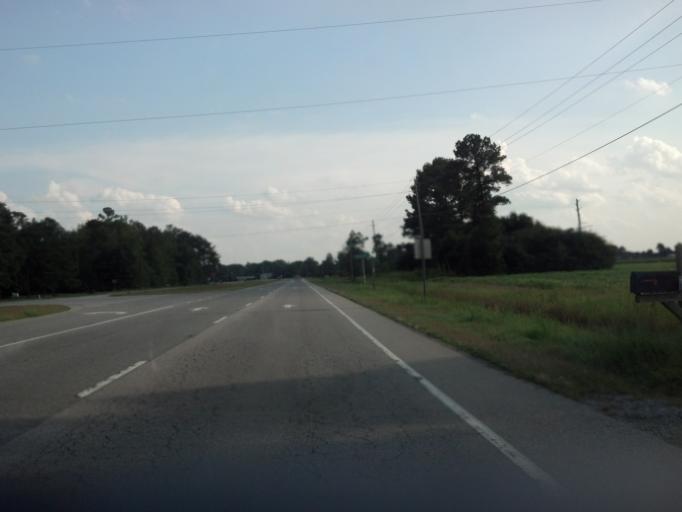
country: US
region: North Carolina
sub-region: Pitt County
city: Greenville
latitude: 35.6813
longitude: -77.3653
